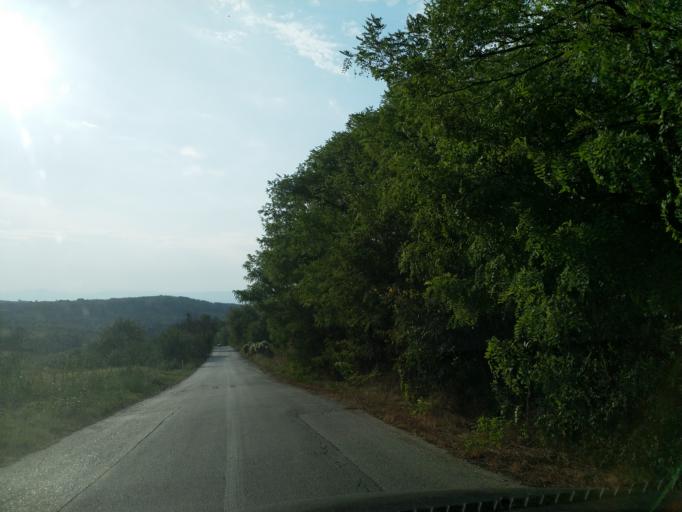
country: RS
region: Central Serbia
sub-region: Pomoravski Okrug
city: Paracin
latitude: 43.8410
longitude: 21.5369
